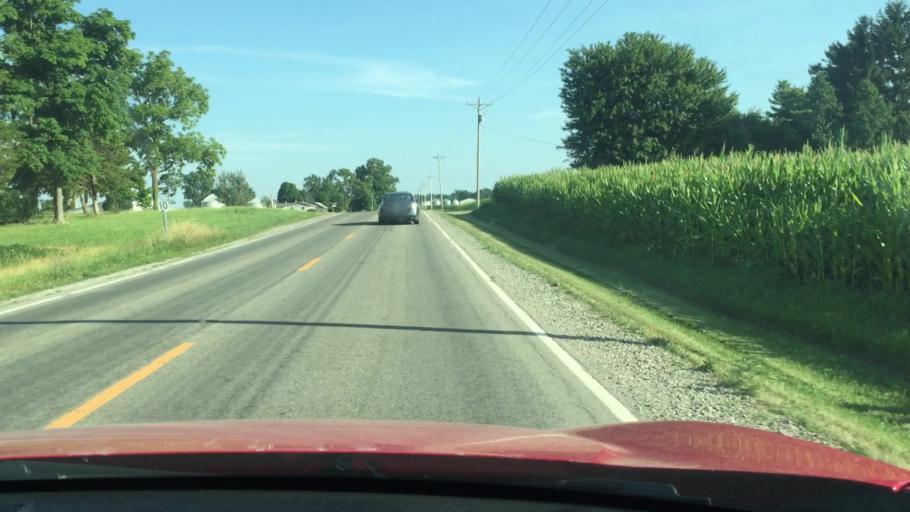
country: US
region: Ohio
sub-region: Hardin County
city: Ada
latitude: 40.6668
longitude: -83.8536
